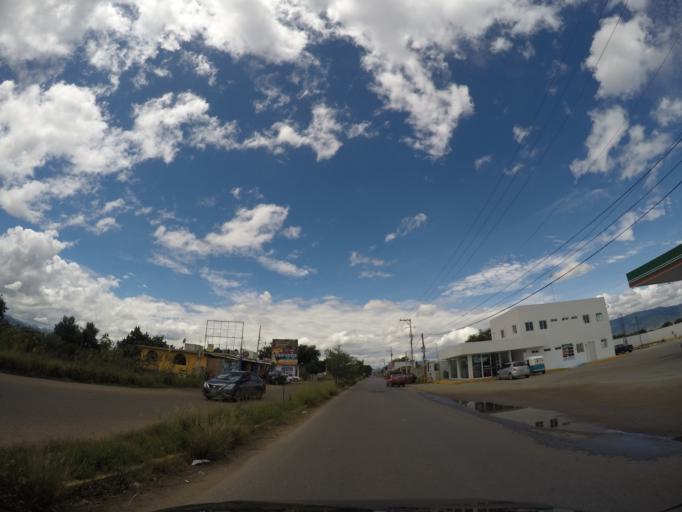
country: MX
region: Oaxaca
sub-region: Santa Cruz Xoxocotlan
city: San Isidro Monjas
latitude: 16.9964
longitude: -96.7420
